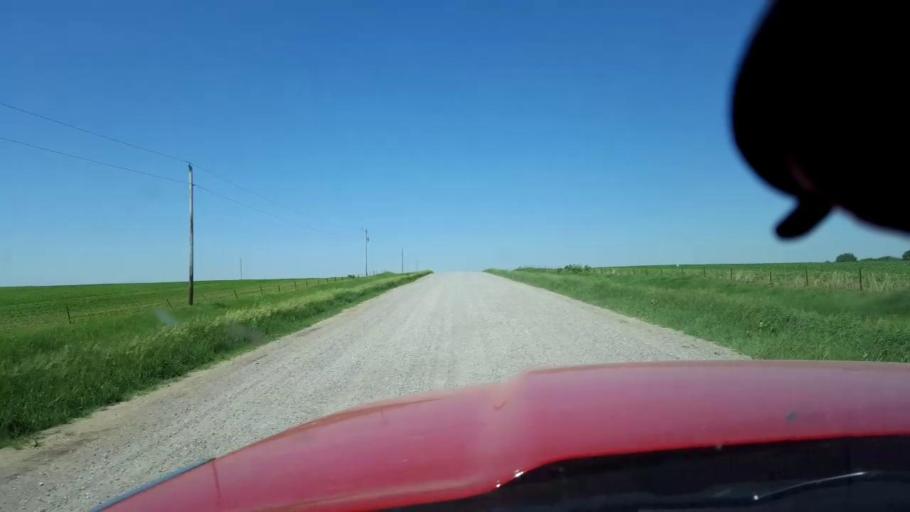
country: US
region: Iowa
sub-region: Chickasaw County
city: New Hampton
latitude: 43.2134
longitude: -92.2404
